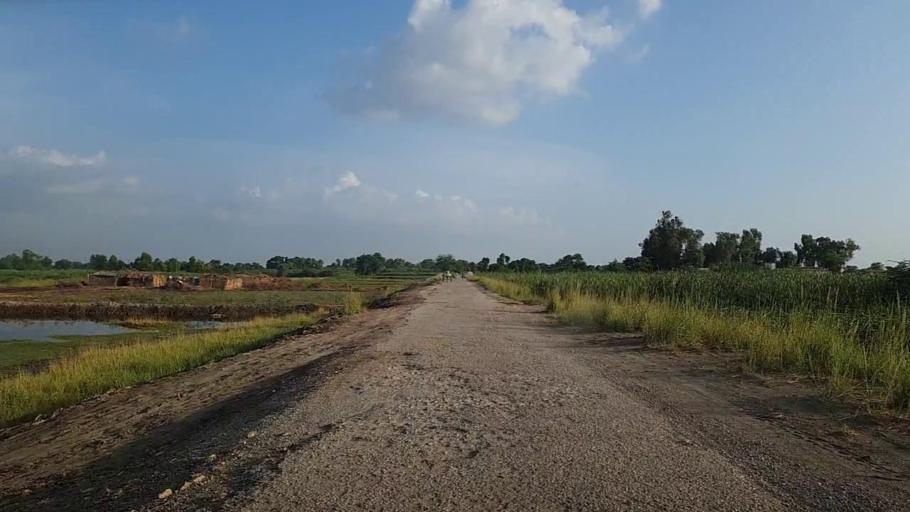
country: PK
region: Sindh
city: Hingorja
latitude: 27.0667
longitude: 68.4188
